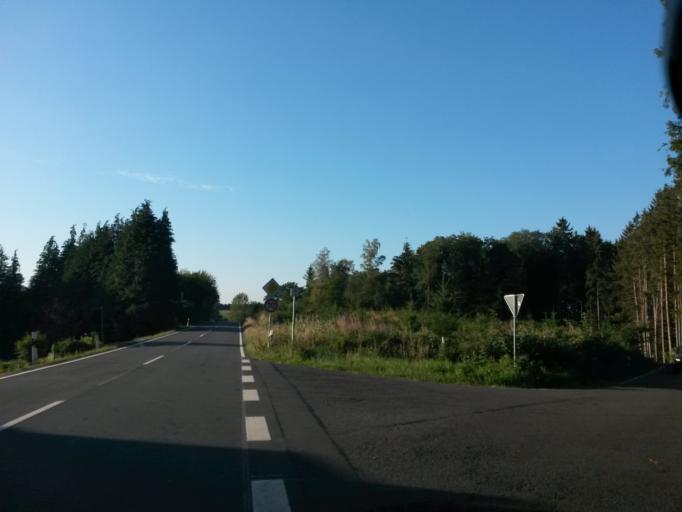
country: DE
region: North Rhine-Westphalia
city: Wipperfurth
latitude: 51.0860
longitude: 7.4052
